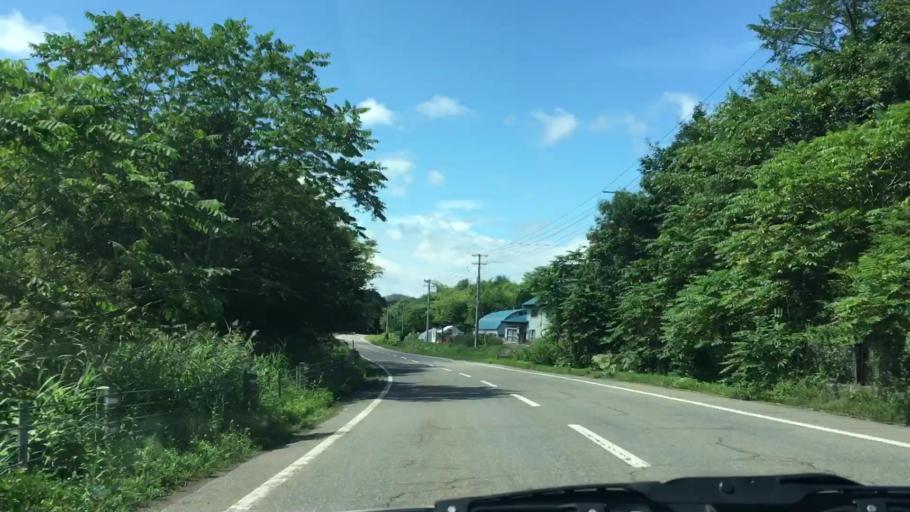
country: JP
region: Hokkaido
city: Otofuke
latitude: 43.2873
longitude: 143.6515
